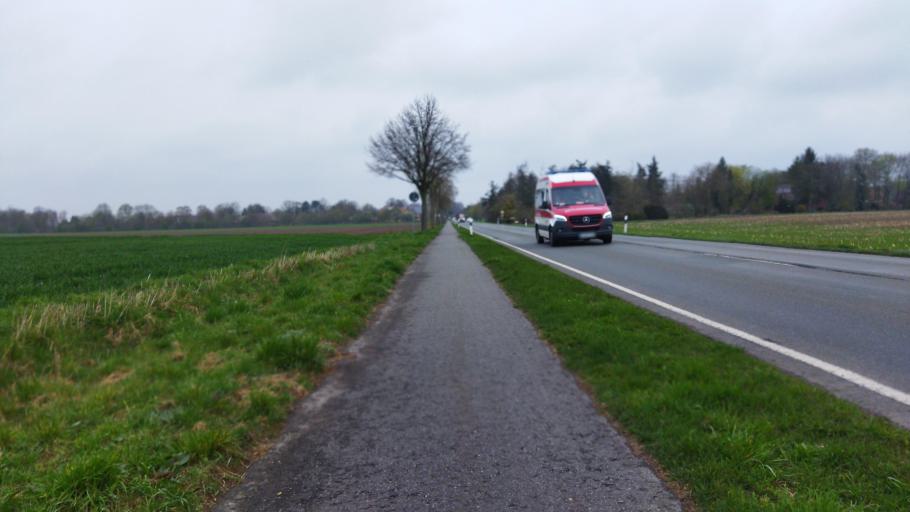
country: DE
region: Lower Saxony
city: Schweringen
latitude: 52.7409
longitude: 9.1837
